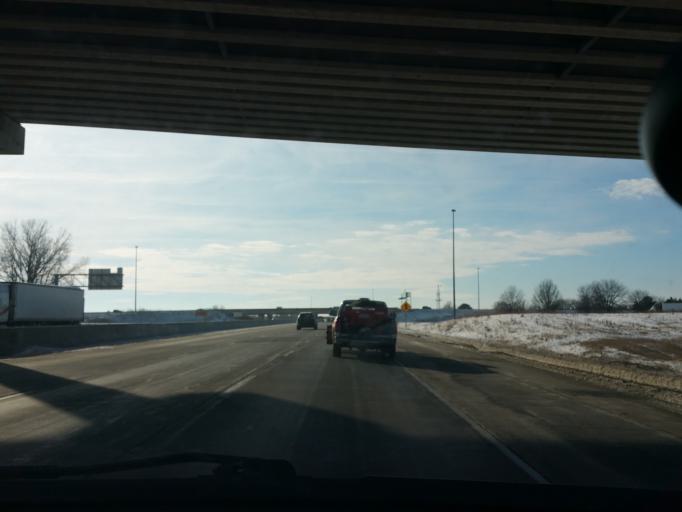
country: US
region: Iowa
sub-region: Polk County
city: Clive
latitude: 41.5957
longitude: -93.7773
